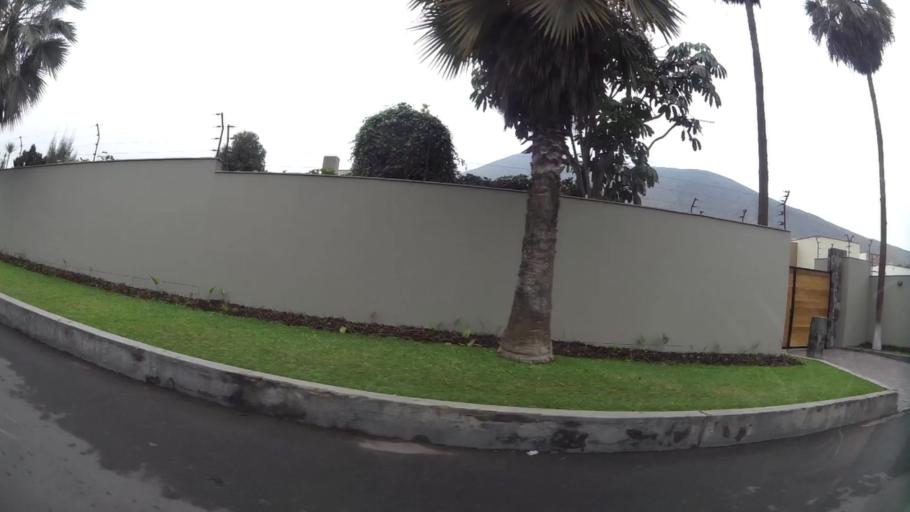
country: PE
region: Lima
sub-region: Lima
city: La Molina
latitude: -12.0831
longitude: -76.9123
